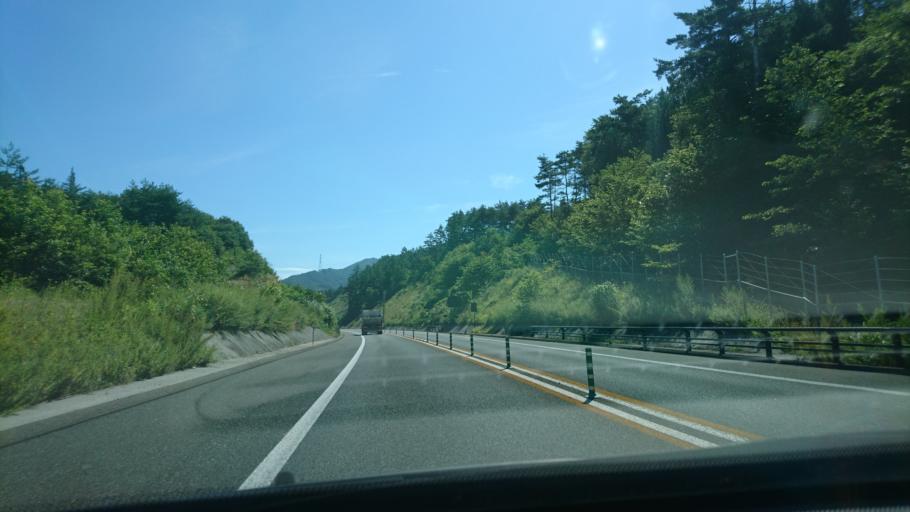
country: JP
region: Iwate
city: Tono
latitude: 39.2892
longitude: 141.3271
